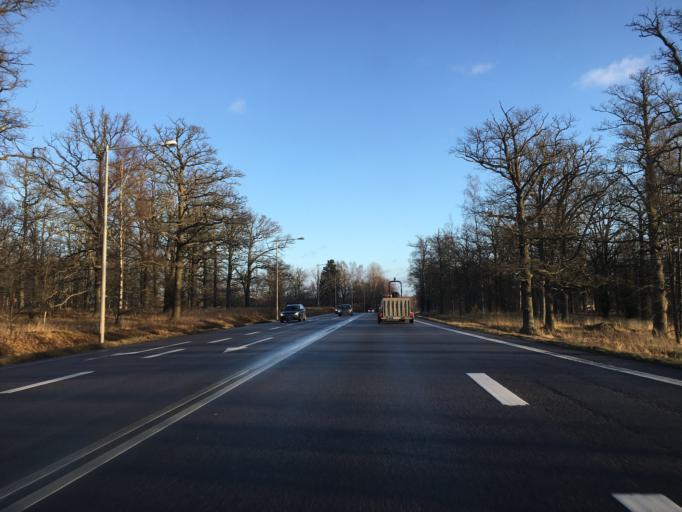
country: SE
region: Kalmar
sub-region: Vasterviks Kommun
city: Vaestervik
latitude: 57.7647
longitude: 16.5630
